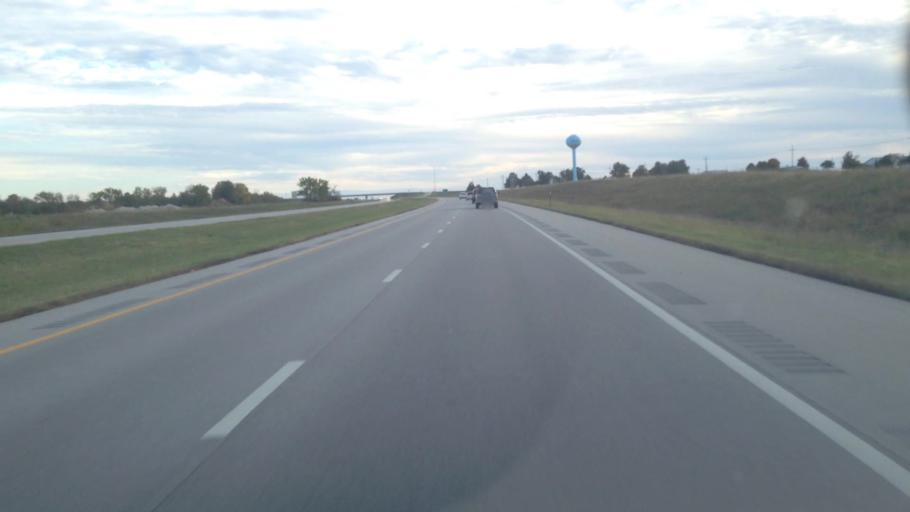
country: US
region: Kansas
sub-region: Douglas County
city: Baldwin City
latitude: 38.8448
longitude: -95.2673
